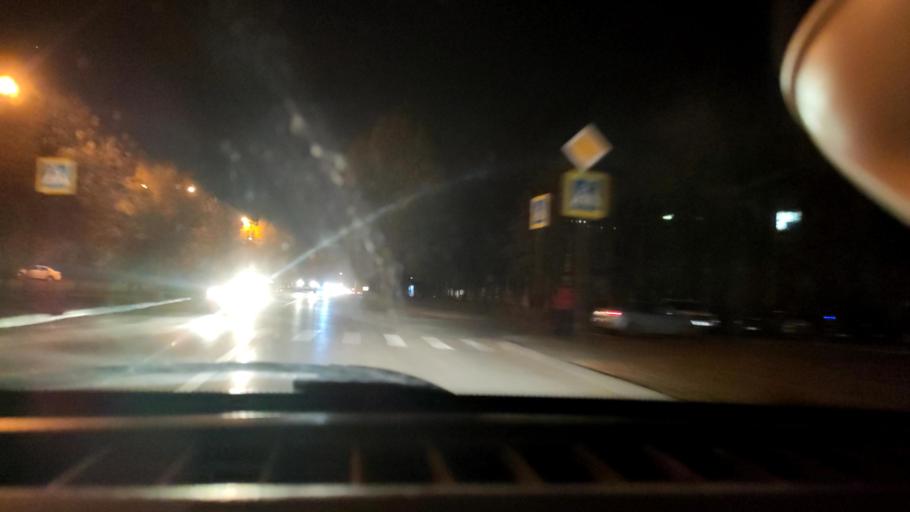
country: RU
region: Samara
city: Samara
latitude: 53.2452
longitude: 50.2054
